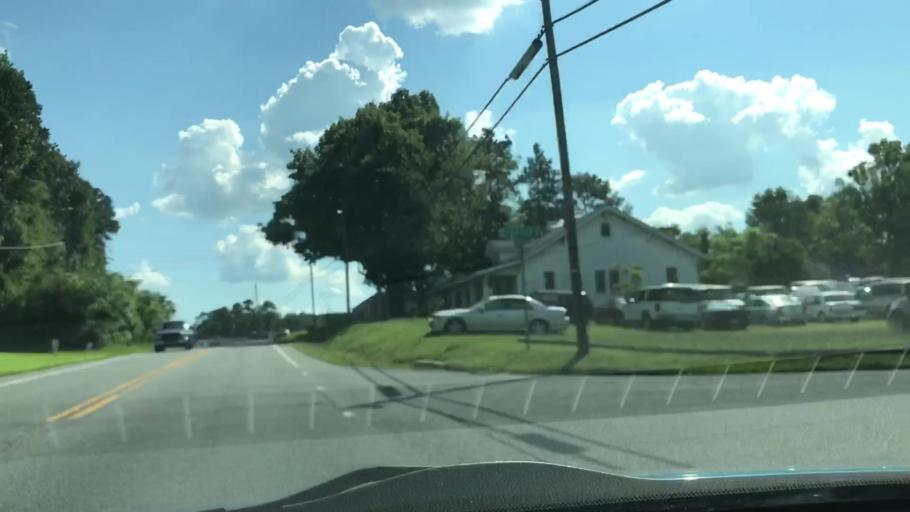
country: US
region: North Carolina
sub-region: Randolph County
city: Asheboro
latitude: 35.7432
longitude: -79.8079
